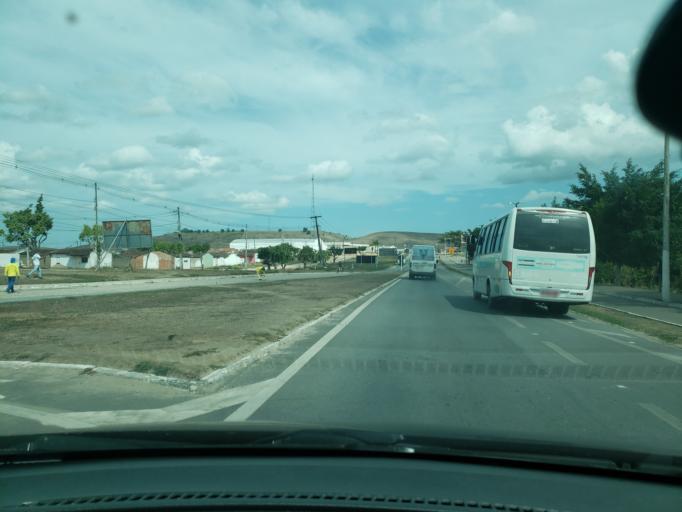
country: BR
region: Alagoas
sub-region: Murici
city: Murici
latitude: -9.3070
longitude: -35.9405
